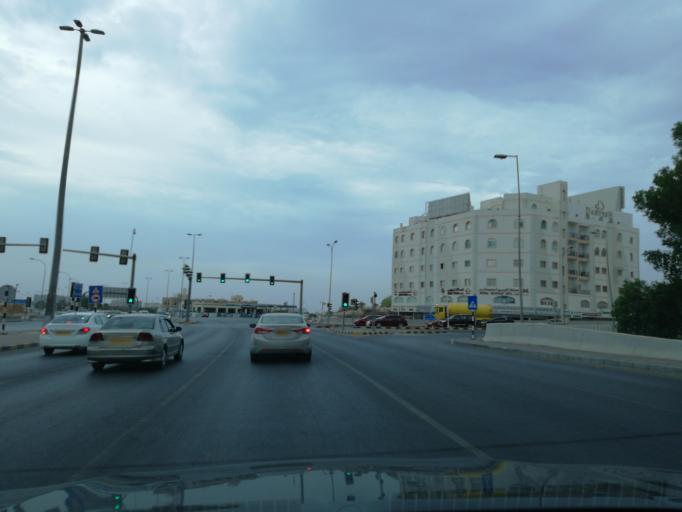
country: OM
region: Muhafazat Masqat
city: Bawshar
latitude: 23.5745
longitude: 58.3827
